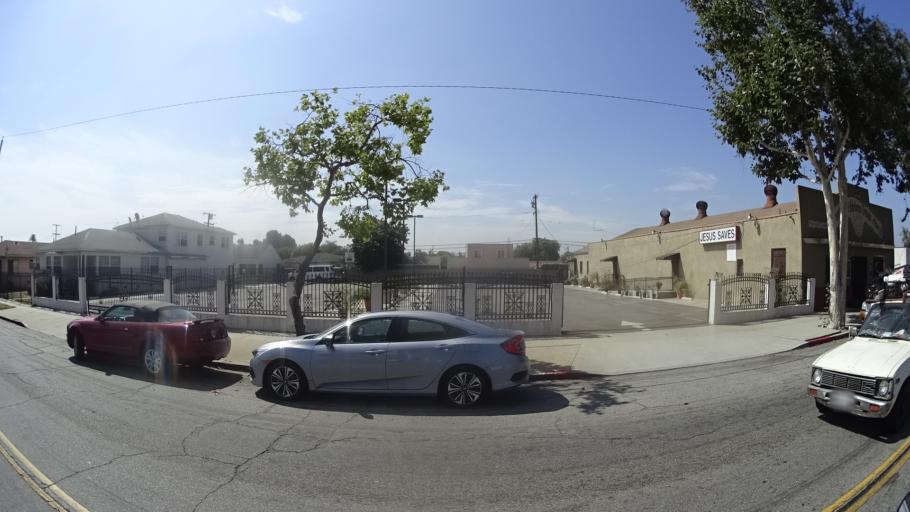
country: US
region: California
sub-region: Los Angeles County
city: View Park-Windsor Hills
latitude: 33.9794
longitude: -118.3400
